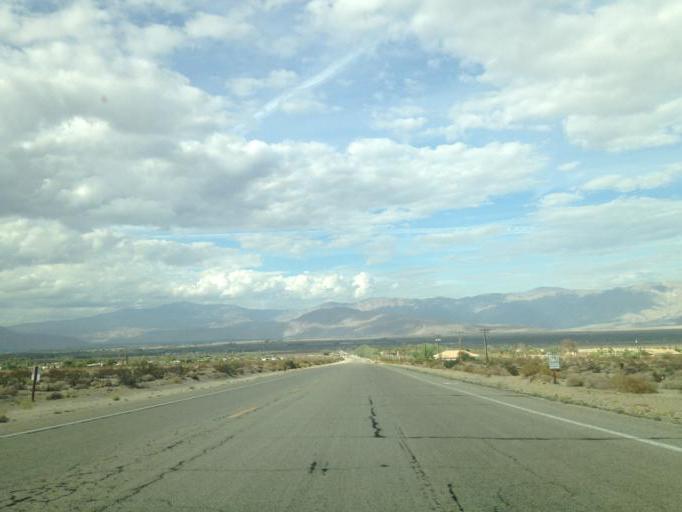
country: US
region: California
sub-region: San Diego County
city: Borrego Springs
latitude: 33.1987
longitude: -116.3302
